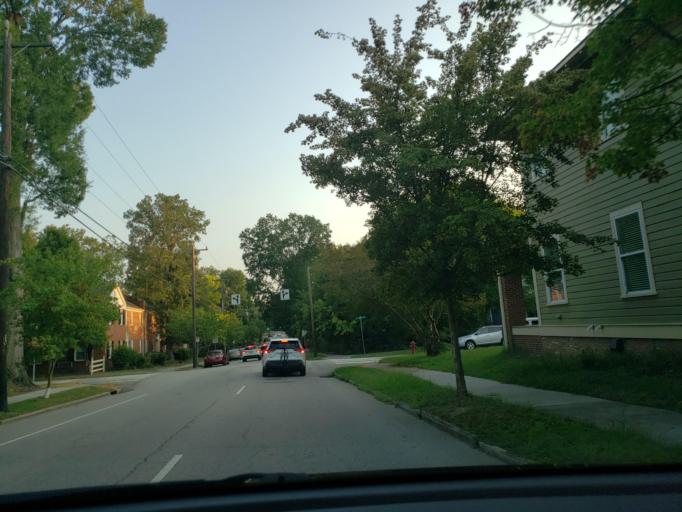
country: US
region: North Carolina
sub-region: Durham County
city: Durham
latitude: 36.0070
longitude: -78.9083
